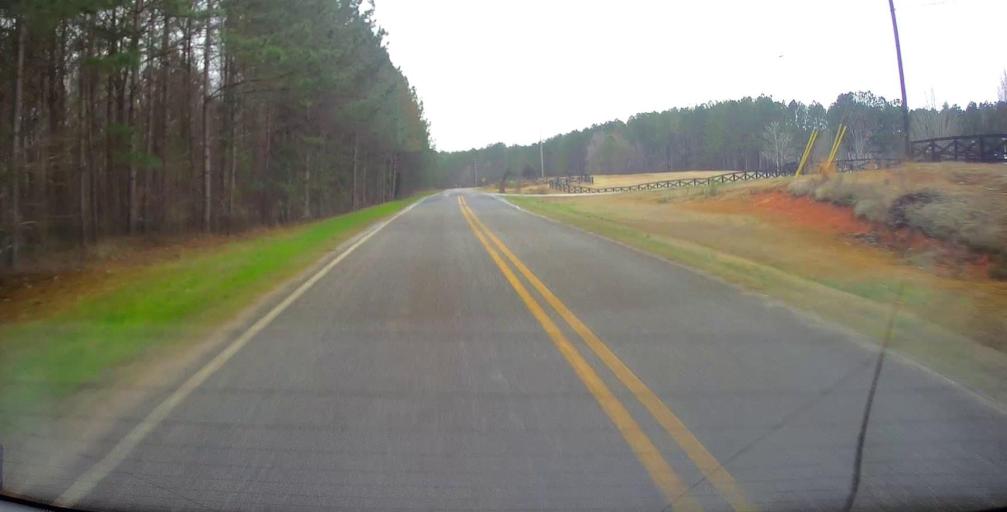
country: US
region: Georgia
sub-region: Monroe County
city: Forsyth
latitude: 33.0025
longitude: -83.8275
